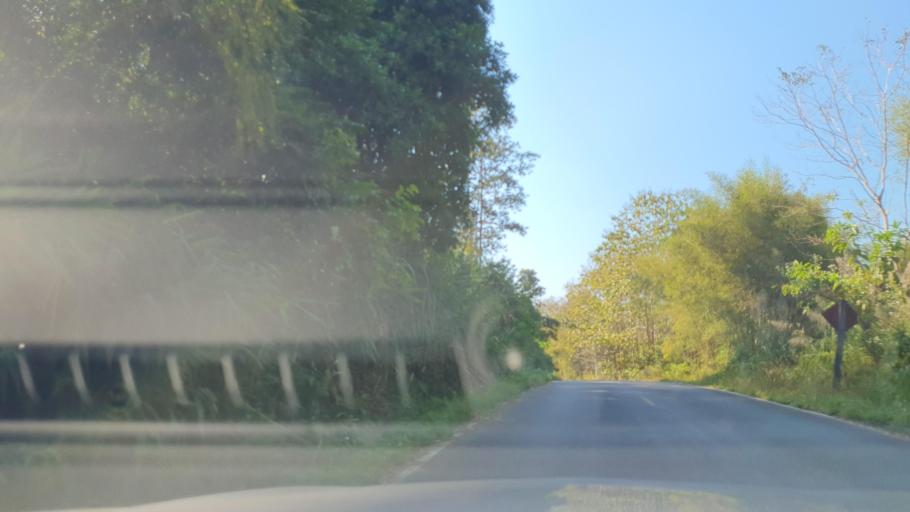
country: TH
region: Nan
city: Pua
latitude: 19.1113
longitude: 100.9086
